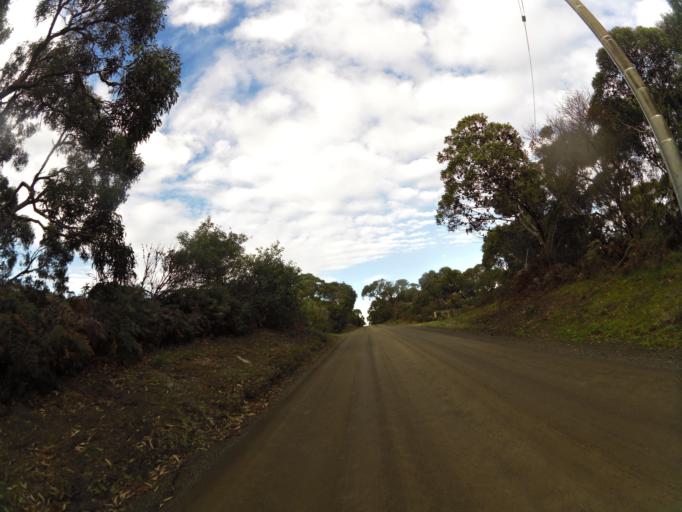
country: AU
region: Victoria
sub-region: Bass Coast
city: North Wonthaggi
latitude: -38.6249
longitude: 145.5654
